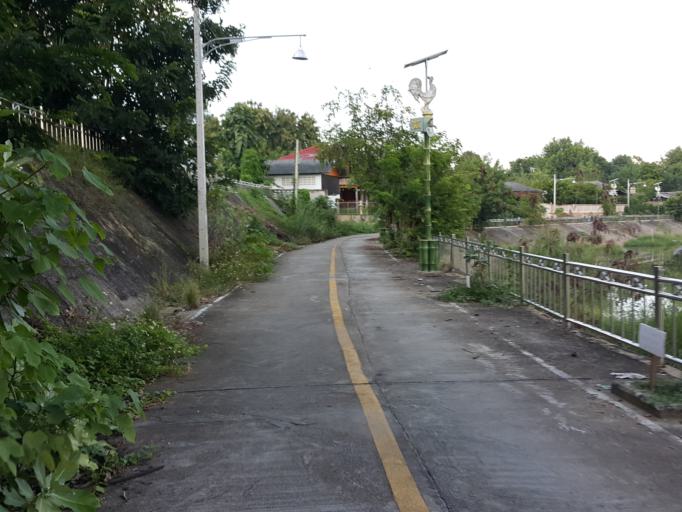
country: TH
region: Lampang
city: Lampang
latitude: 18.3013
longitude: 99.5106
